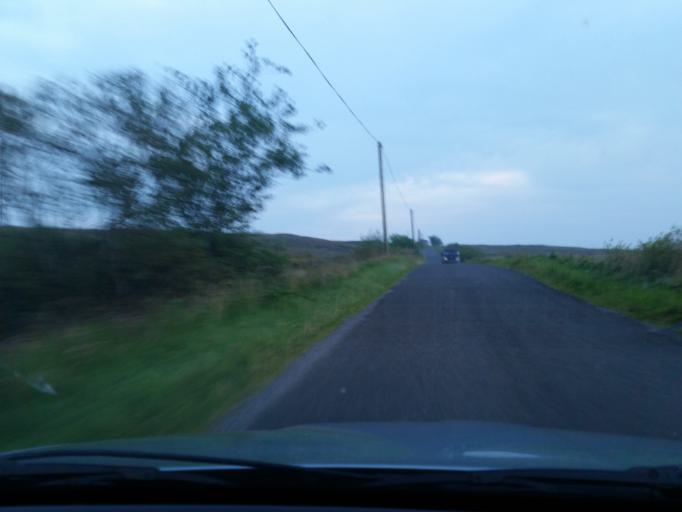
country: IE
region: Ulster
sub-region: County Monaghan
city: Clones
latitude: 54.2745
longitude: -7.2743
